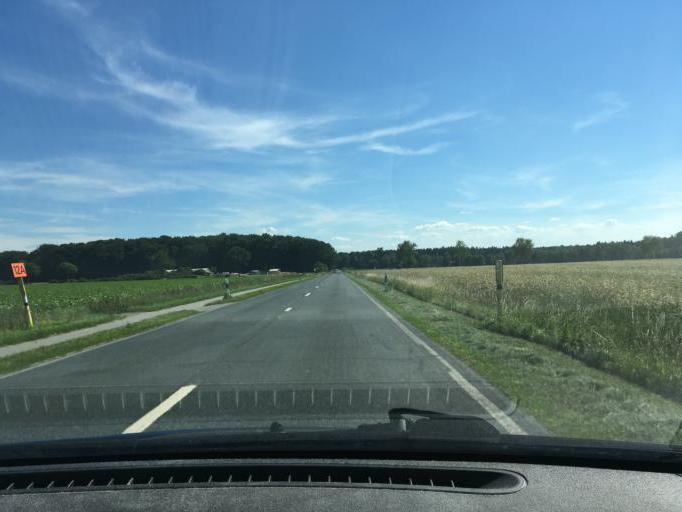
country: DE
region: Lower Saxony
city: Bendestorf
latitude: 53.3585
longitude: 9.9415
